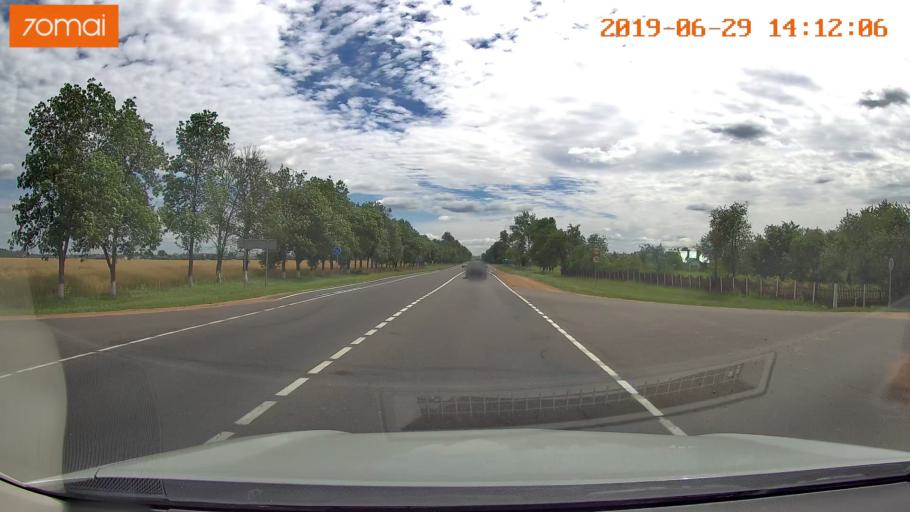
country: BY
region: Minsk
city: Salihorsk
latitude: 52.8133
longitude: 27.5060
